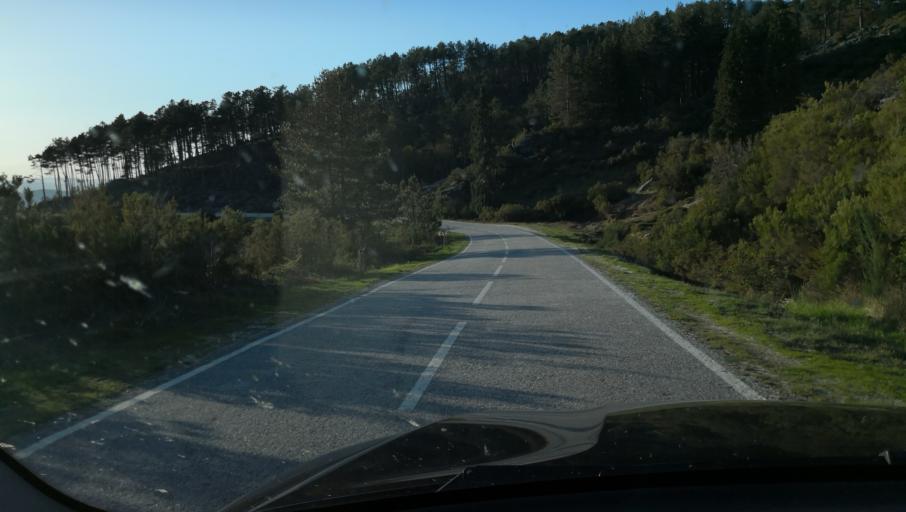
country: PT
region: Vila Real
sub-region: Vila Real
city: Vila Real
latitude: 41.3863
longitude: -7.8234
